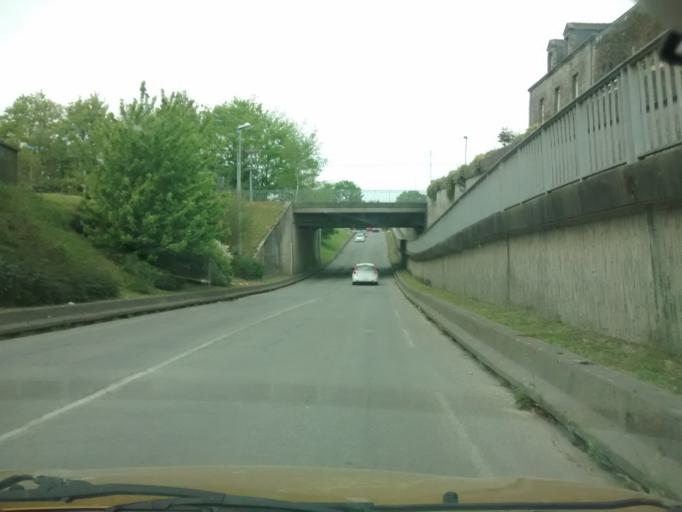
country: FR
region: Brittany
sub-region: Departement du Morbihan
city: Questembert
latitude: 47.6826
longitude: -2.4488
